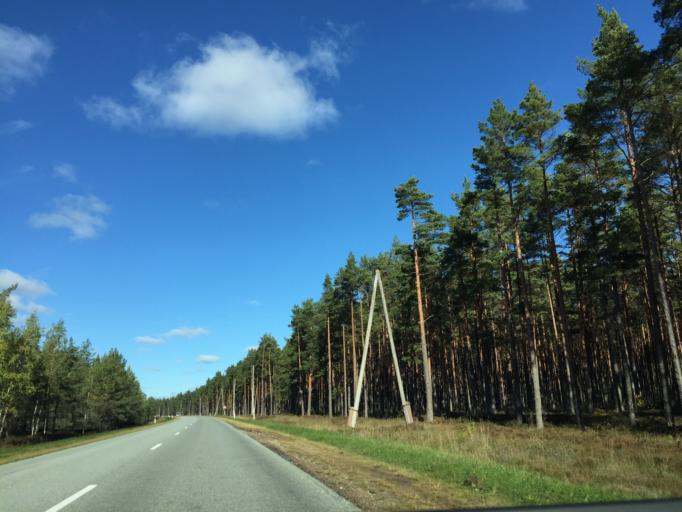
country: LV
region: Mesraga
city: Mersrags
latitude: 57.2583
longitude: 23.1728
